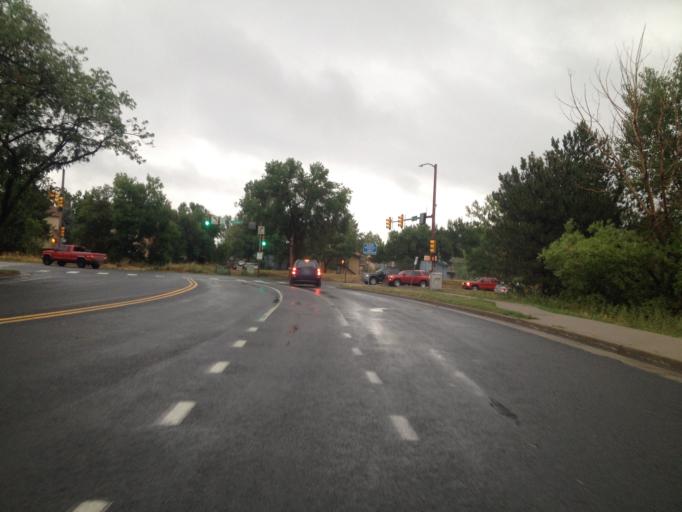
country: US
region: Colorado
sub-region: Boulder County
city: Louisville
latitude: 39.9864
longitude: -105.1422
